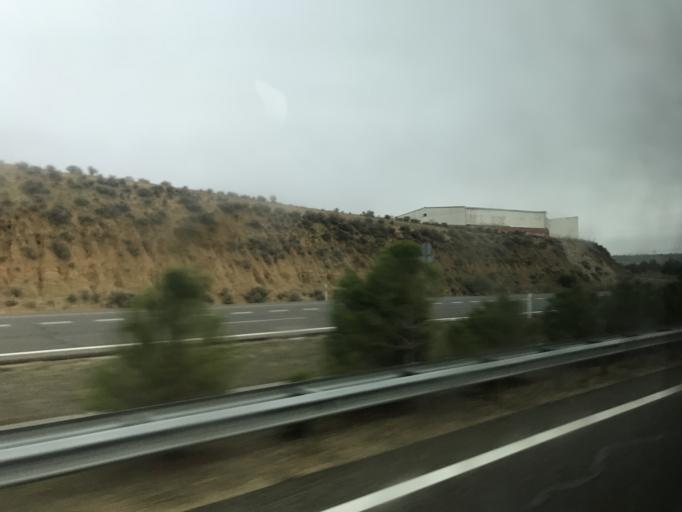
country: ES
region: Castille and Leon
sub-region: Provincia de Palencia
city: Villalobon
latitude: 42.0368
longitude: -4.5227
